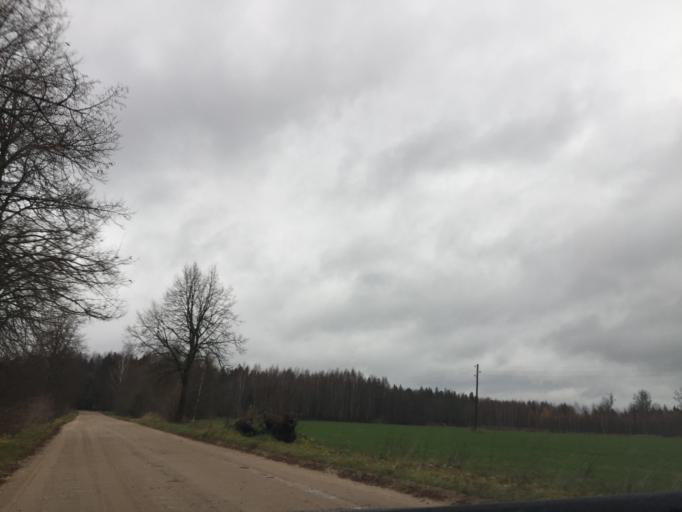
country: LV
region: Limbazu Rajons
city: Limbazi
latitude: 57.5555
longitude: 24.8096
